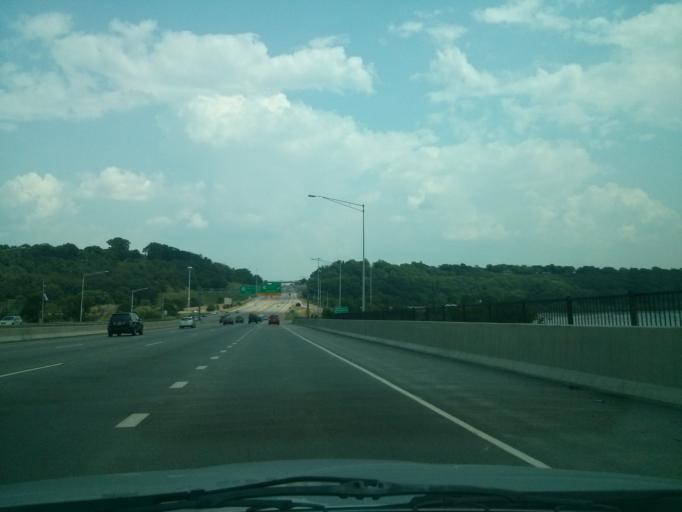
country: US
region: Minnesota
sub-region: Washington County
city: Lakeland
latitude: 44.9626
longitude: -92.7596
